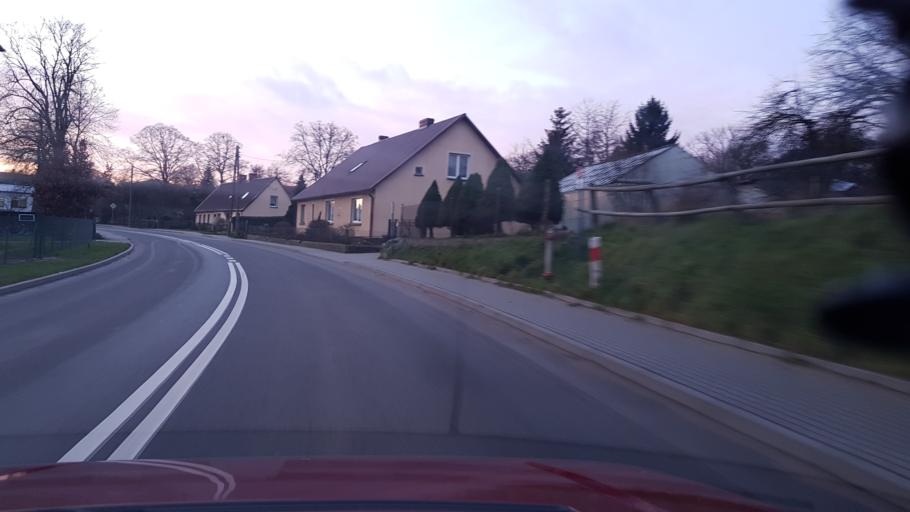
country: PL
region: Pomeranian Voivodeship
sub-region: Powiat bytowski
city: Bytow
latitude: 54.1367
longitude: 17.4249
